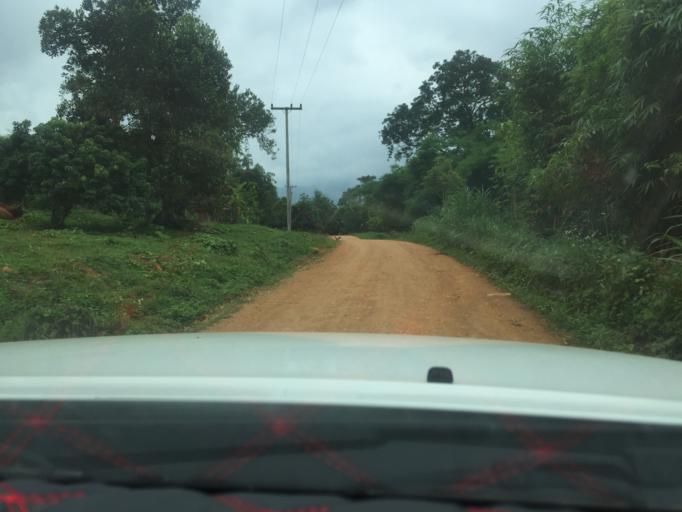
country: TH
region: Phayao
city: Phu Sang
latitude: 19.7371
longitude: 100.4710
